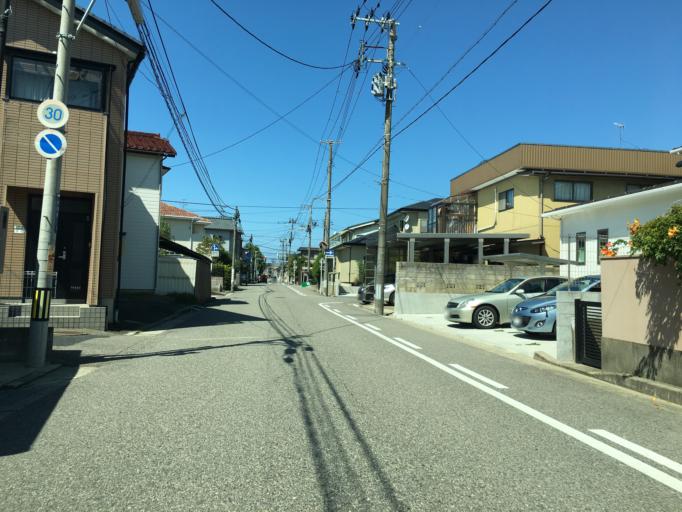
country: JP
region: Niigata
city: Niigata-shi
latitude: 37.9053
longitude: 139.0098
